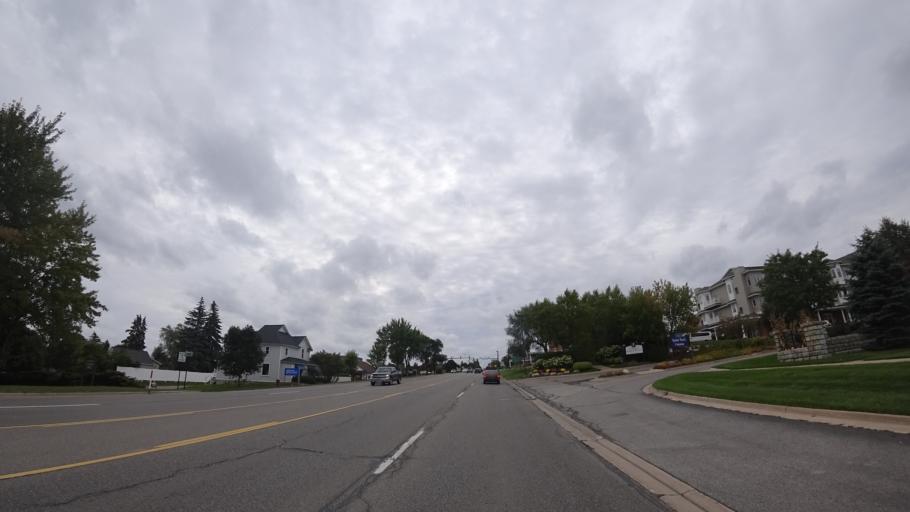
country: US
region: Michigan
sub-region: Emmet County
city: Petoskey
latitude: 45.3645
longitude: -84.9710
